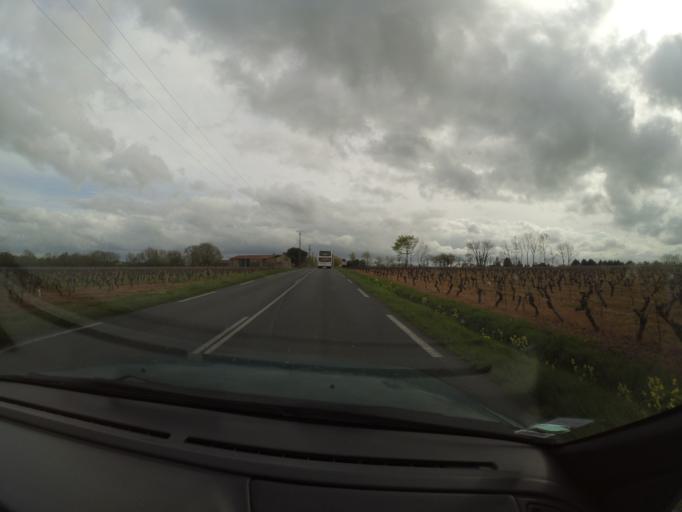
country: FR
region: Pays de la Loire
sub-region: Departement de Maine-et-Loire
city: Lire
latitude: 47.3167
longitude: -1.1634
